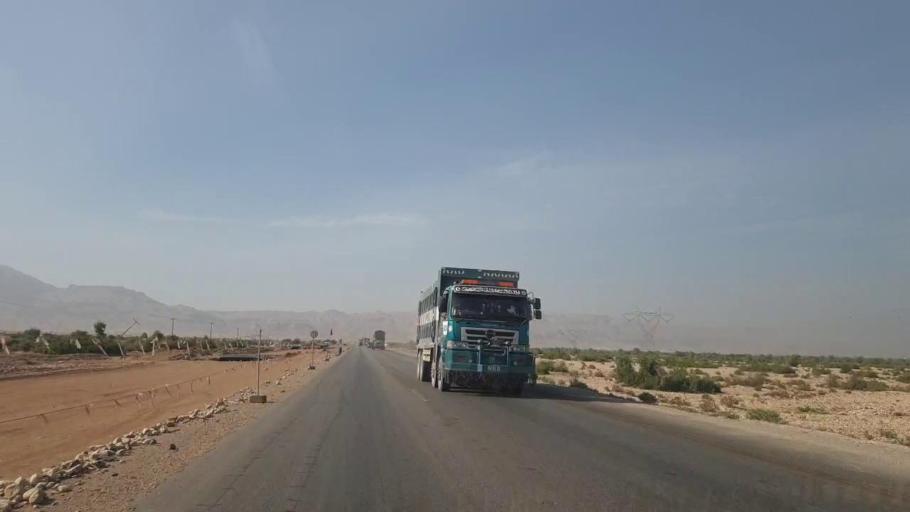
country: PK
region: Sindh
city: Sehwan
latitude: 26.2128
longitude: 67.9201
